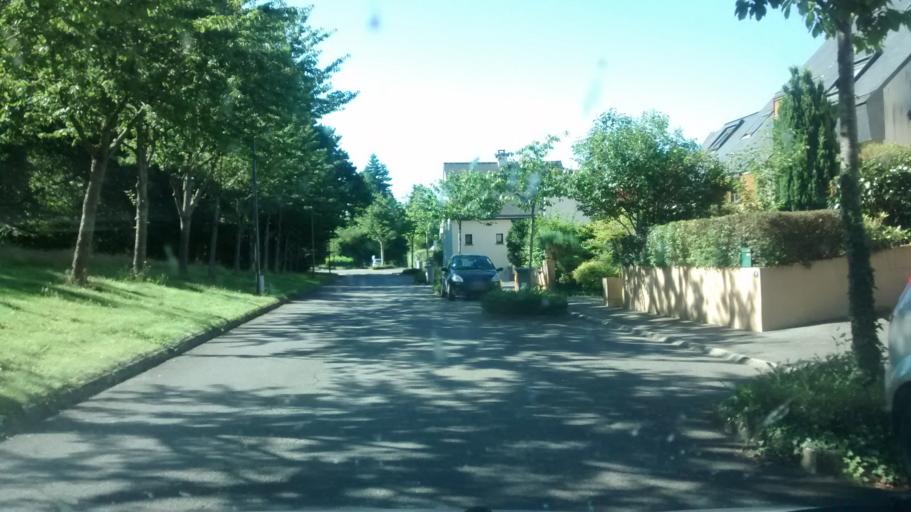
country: FR
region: Brittany
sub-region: Departement d'Ille-et-Vilaine
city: Chantepie
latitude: 48.0940
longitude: -1.6150
